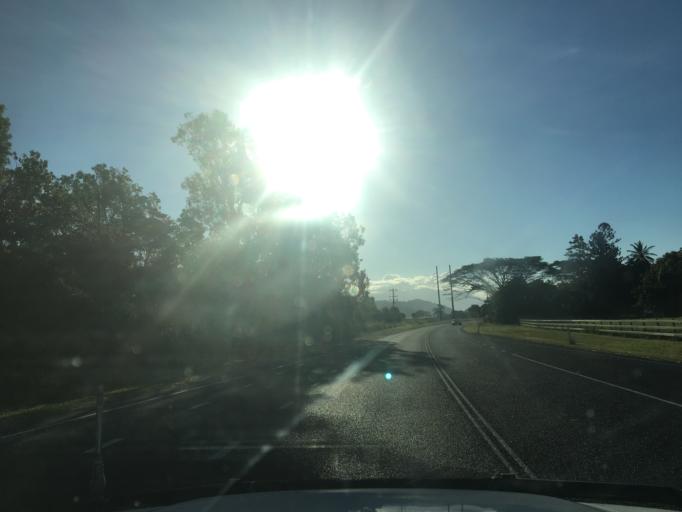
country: AU
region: Queensland
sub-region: Cairns
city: Port Douglas
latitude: -16.5217
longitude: 145.4519
